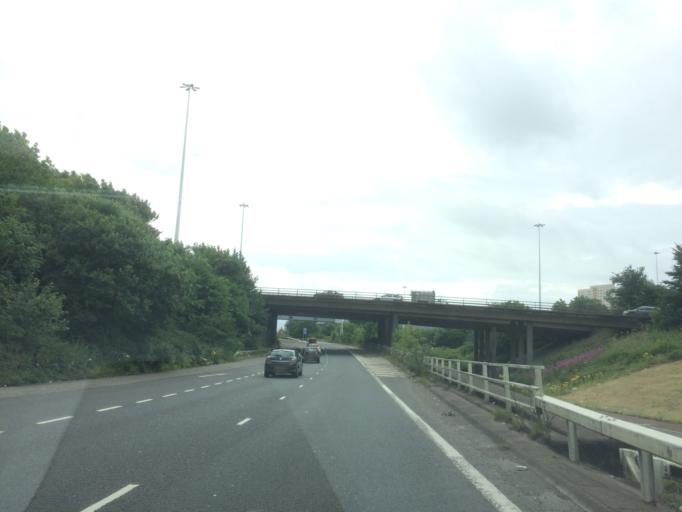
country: GB
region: Scotland
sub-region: Glasgow City
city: Glasgow
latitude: 55.8686
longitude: -4.2353
